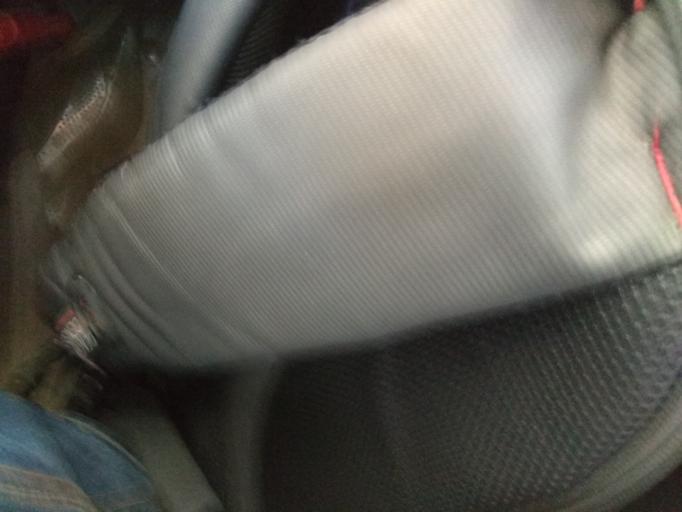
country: MM
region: Mandalay
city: Nay Pyi Taw
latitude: 19.8154
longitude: 96.1534
